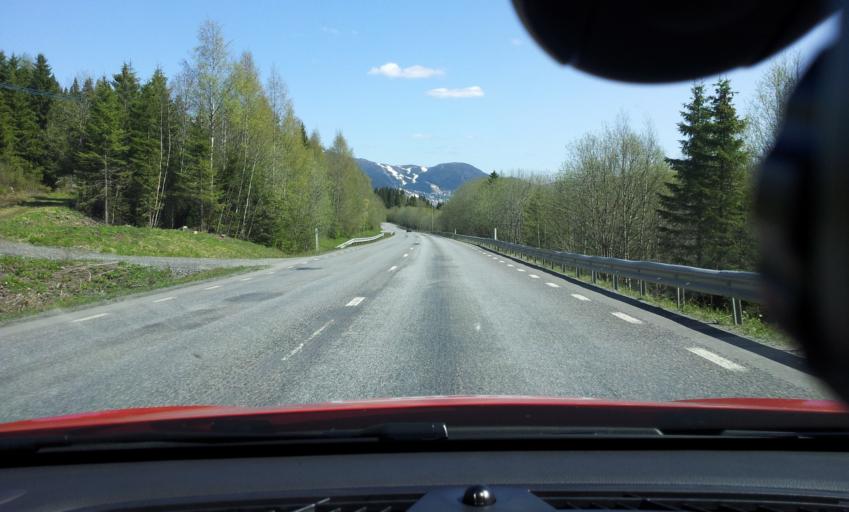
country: SE
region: Jaemtland
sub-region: Are Kommun
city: Are
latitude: 63.3951
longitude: 12.9462
